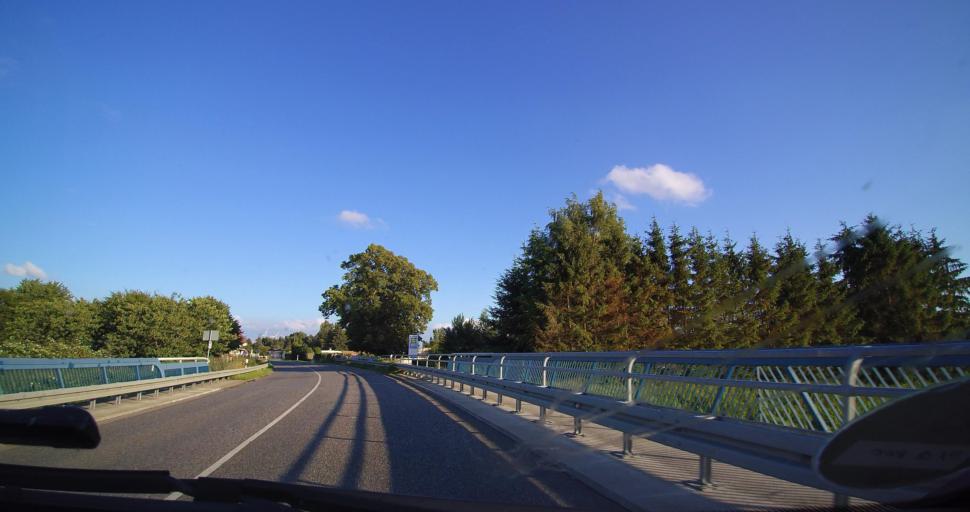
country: DE
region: Mecklenburg-Vorpommern
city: Tribsees
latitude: 54.0965
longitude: 12.7518
